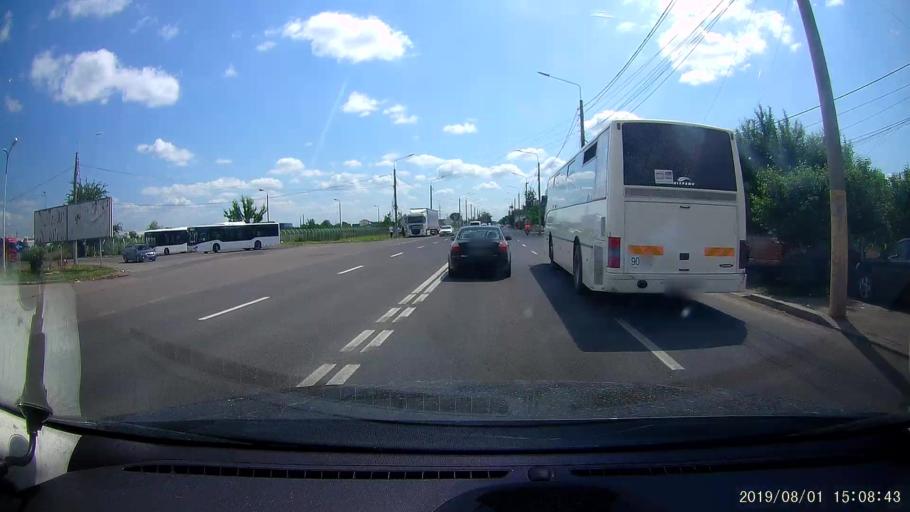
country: RO
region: Braila
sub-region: Municipiul Braila
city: Braila
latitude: 45.2393
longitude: 27.9435
